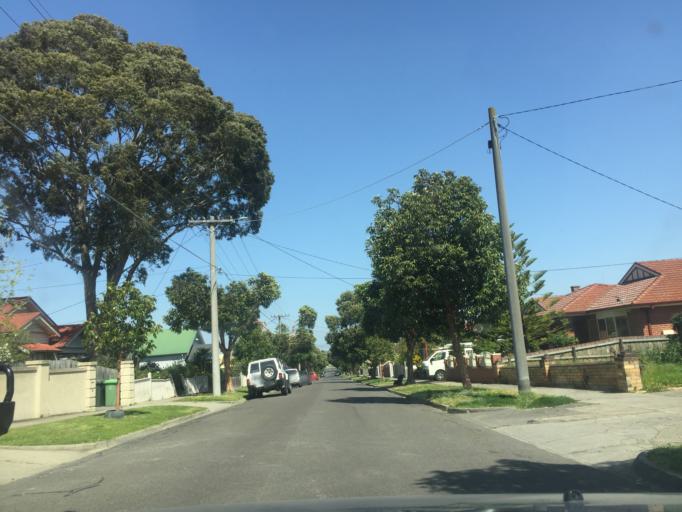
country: AU
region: Victoria
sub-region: Darebin
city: Preston
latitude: -37.7368
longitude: 145.0203
